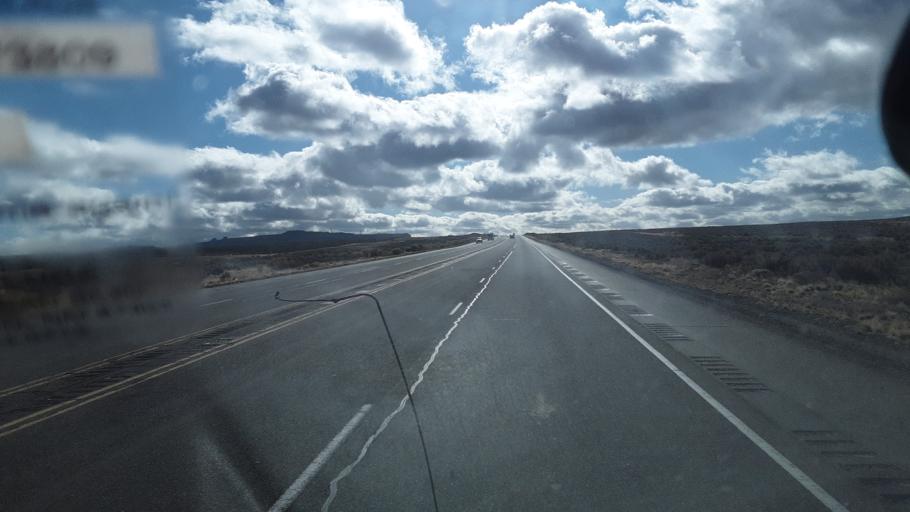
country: US
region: New Mexico
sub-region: San Juan County
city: Bloomfield
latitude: 36.4658
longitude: -107.9050
